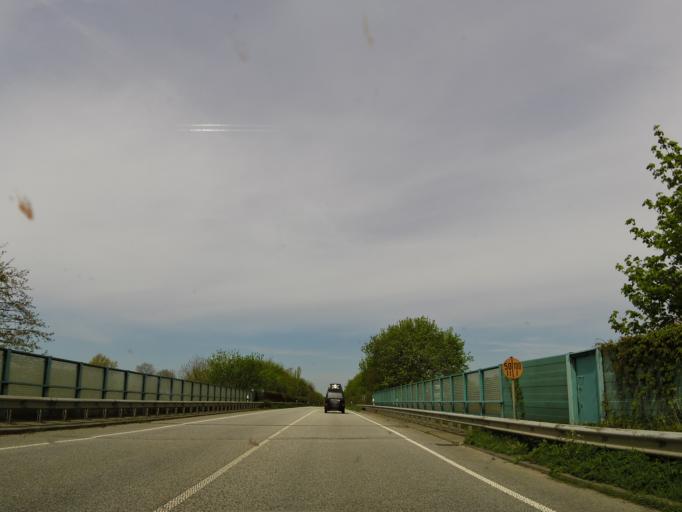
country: DE
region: Schleswig-Holstein
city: Groven
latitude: 54.2906
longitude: 8.9823
